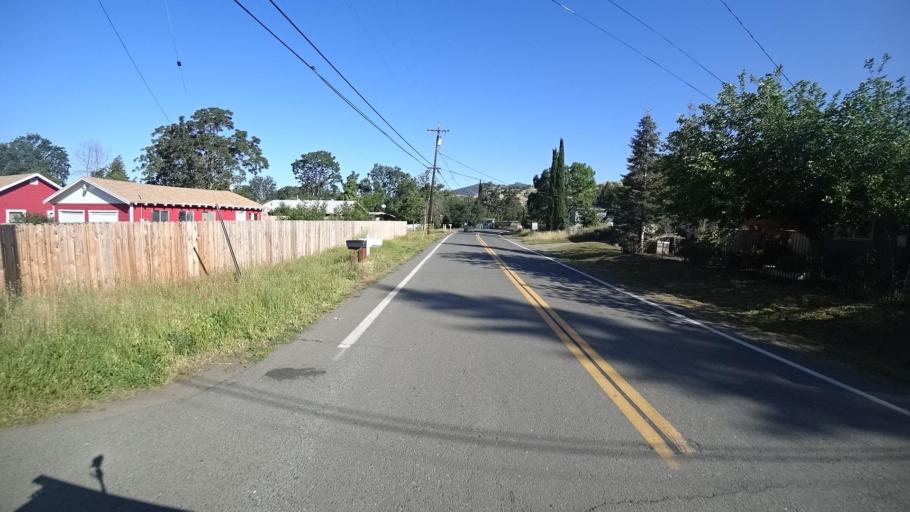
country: US
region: California
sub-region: Lake County
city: Lucerne
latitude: 39.0932
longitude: -122.7946
